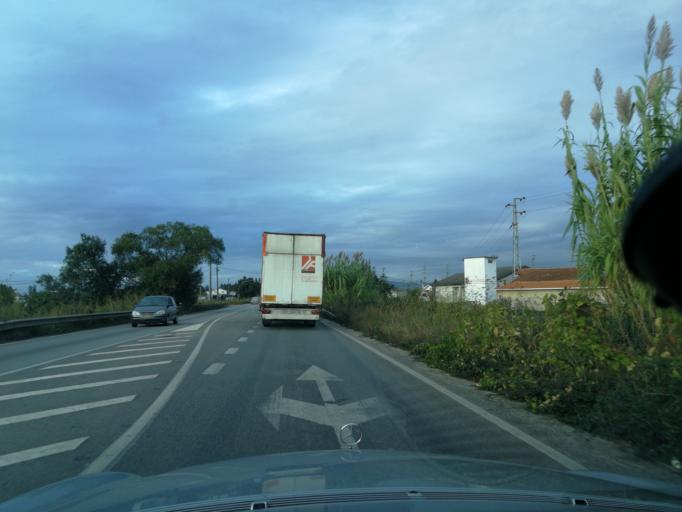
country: PT
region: Aveiro
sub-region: Agueda
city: Valongo
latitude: 40.6172
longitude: -8.4629
